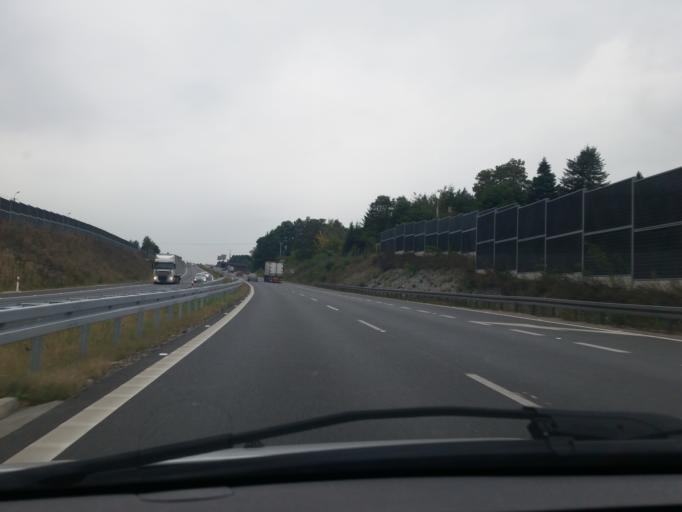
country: PL
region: Masovian Voivodeship
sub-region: Powiat zyrardowski
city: Mszczonow
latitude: 51.9751
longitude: 20.5045
